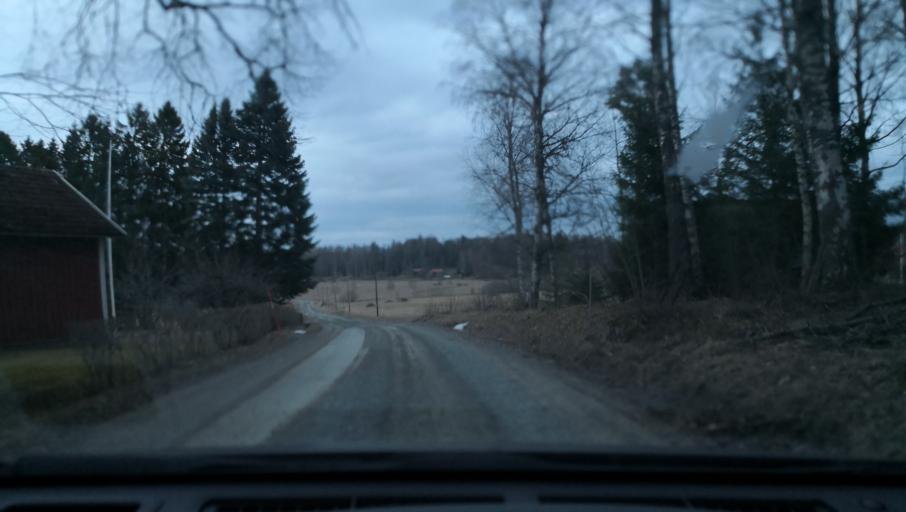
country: SE
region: Vaestmanland
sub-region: Kopings Kommun
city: Kolsva
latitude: 59.5879
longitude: 15.7153
